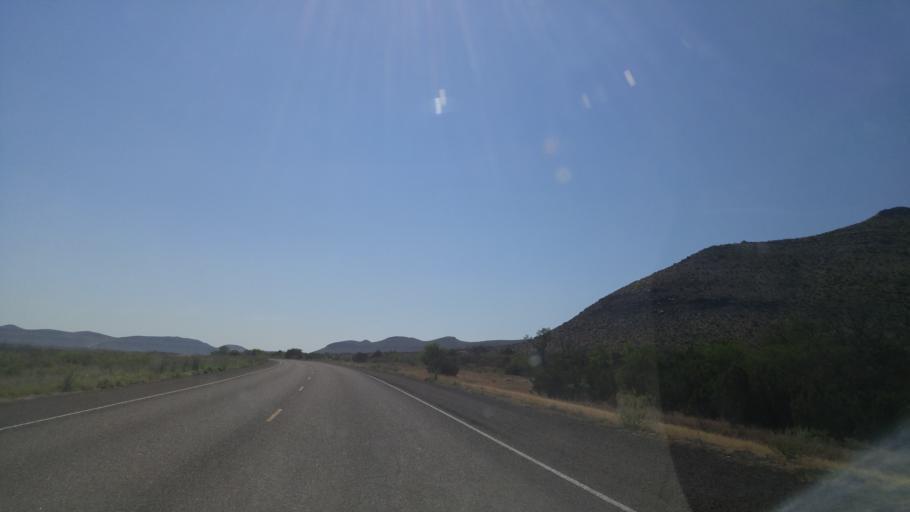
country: US
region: Texas
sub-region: Terrell County
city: Sanderson
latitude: 30.1753
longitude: -102.7646
